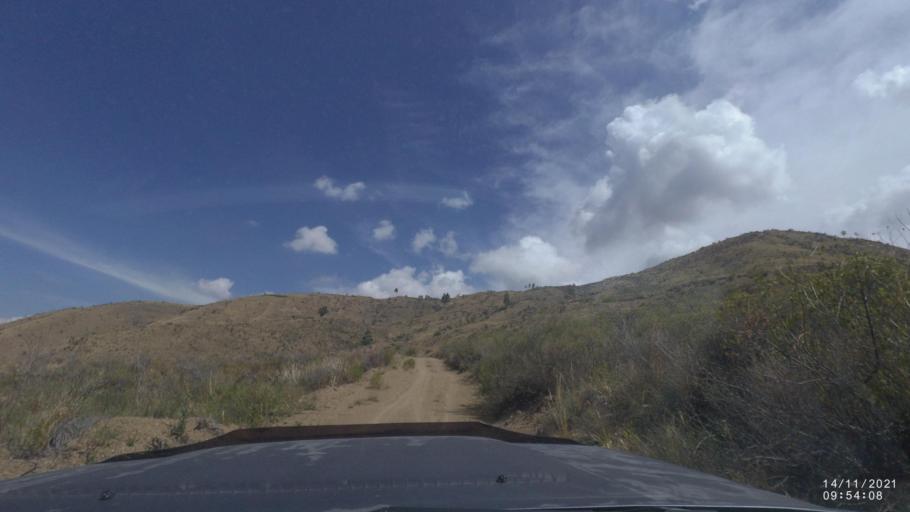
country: BO
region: Cochabamba
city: Cochabamba
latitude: -17.3593
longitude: -66.0878
